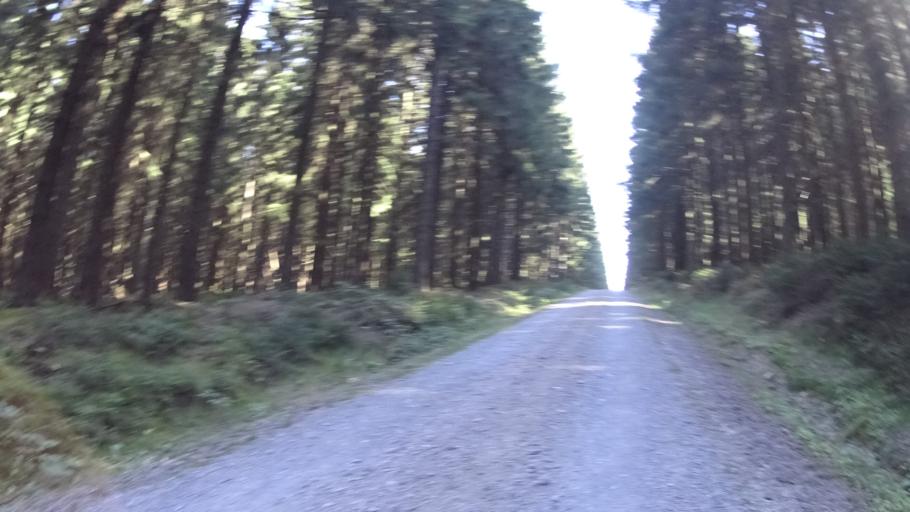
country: DE
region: Thuringia
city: Neustadt am Rennsteig
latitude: 50.6279
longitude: 10.9326
